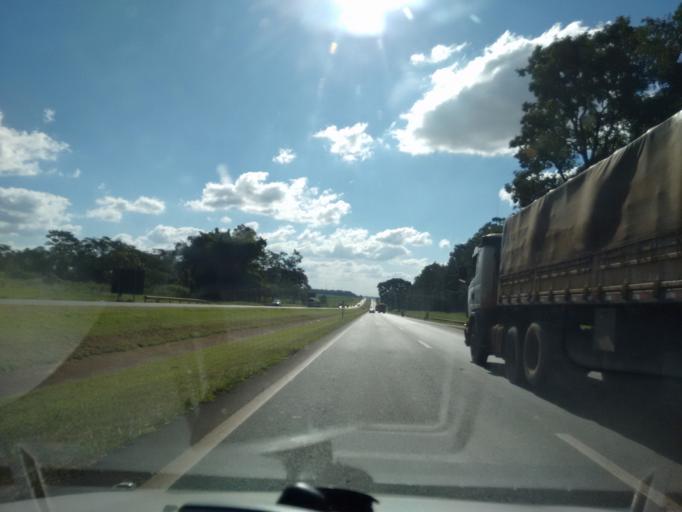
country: BR
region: Sao Paulo
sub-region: Araraquara
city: Araraquara
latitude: -21.8343
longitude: -48.1563
